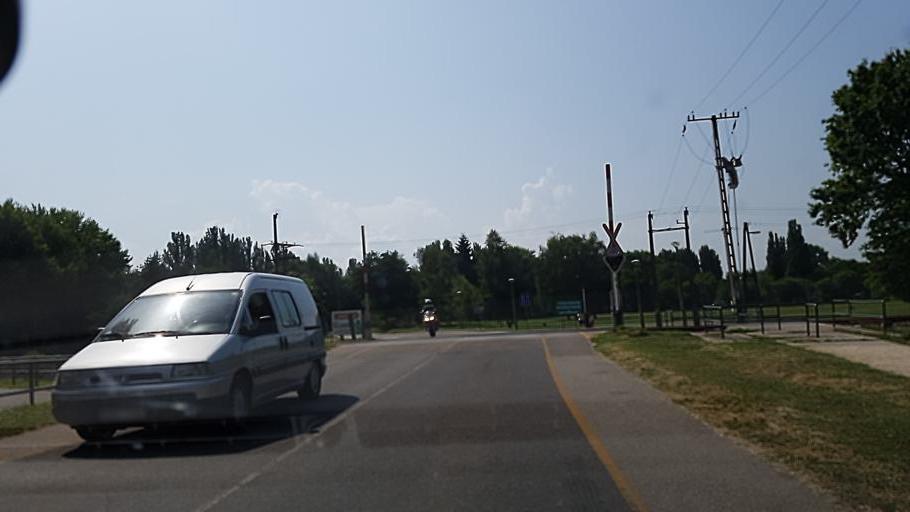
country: HU
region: Jasz-Nagykun-Szolnok
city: Tiszafured
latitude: 47.6216
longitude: 20.7431
